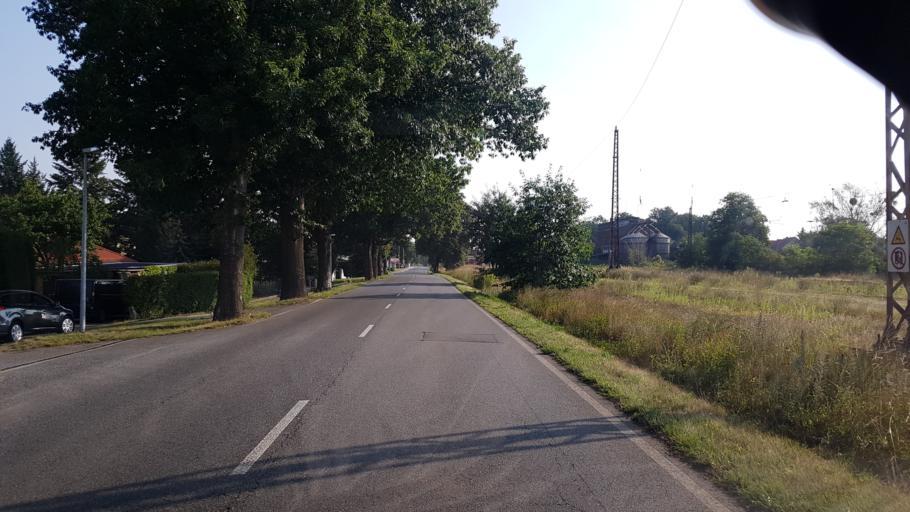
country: DE
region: Brandenburg
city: Drebkau
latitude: 51.6510
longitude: 14.2173
